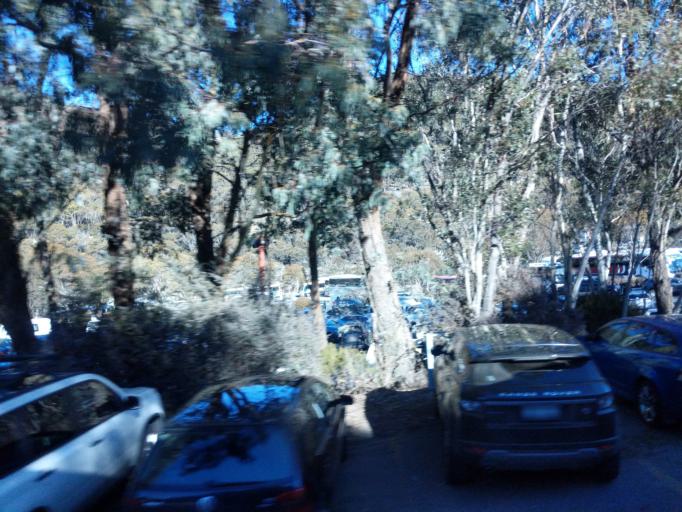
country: AU
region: New South Wales
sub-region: Snowy River
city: Jindabyne
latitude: -36.4985
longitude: 148.3126
